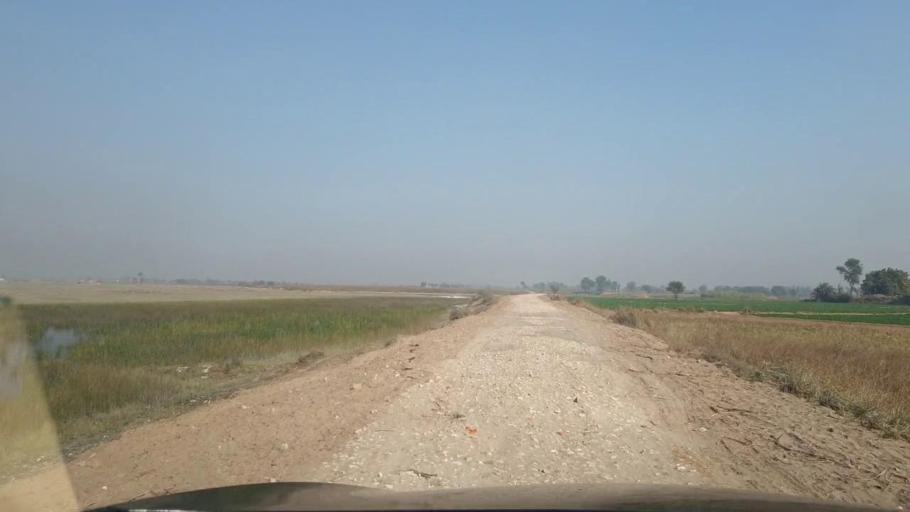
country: PK
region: Sindh
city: Ubauro
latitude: 28.1278
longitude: 69.7502
